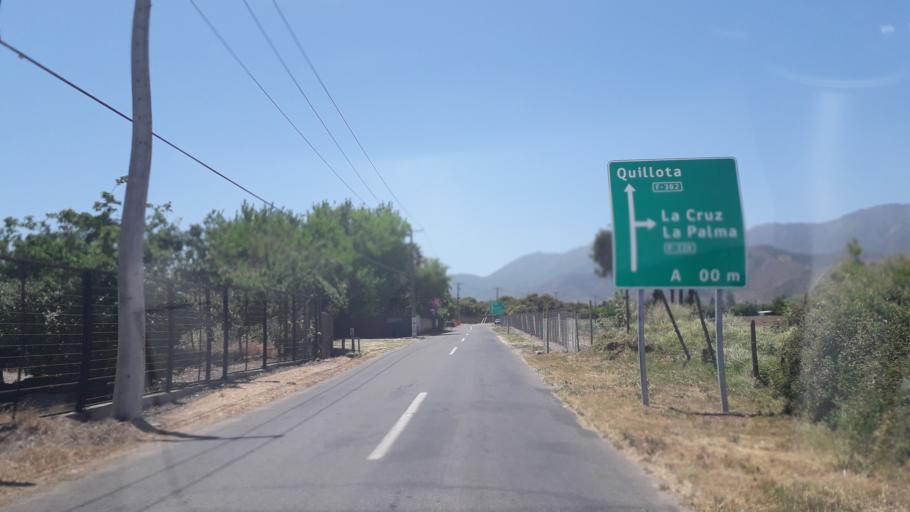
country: CL
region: Valparaiso
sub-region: Provincia de Quillota
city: Quillota
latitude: -32.9099
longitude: -71.2249
